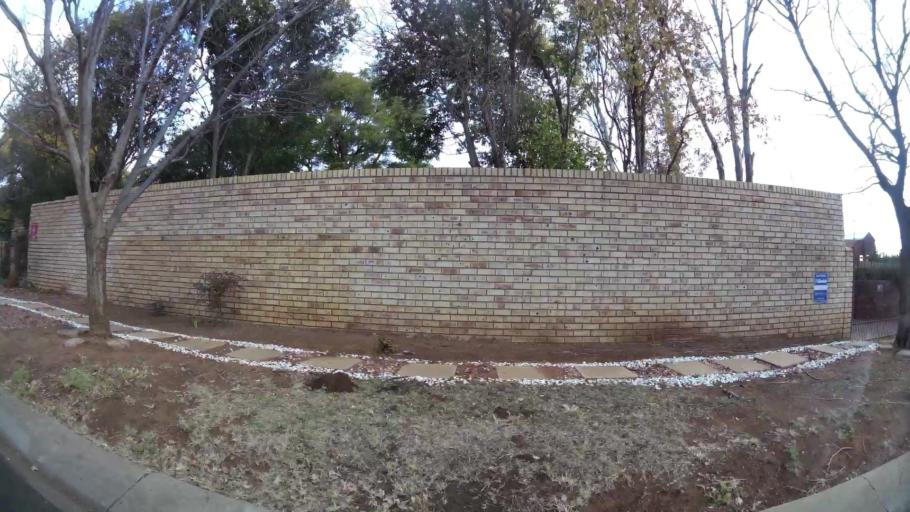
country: ZA
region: Orange Free State
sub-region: Mangaung Metropolitan Municipality
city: Bloemfontein
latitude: -29.0852
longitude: 26.1984
